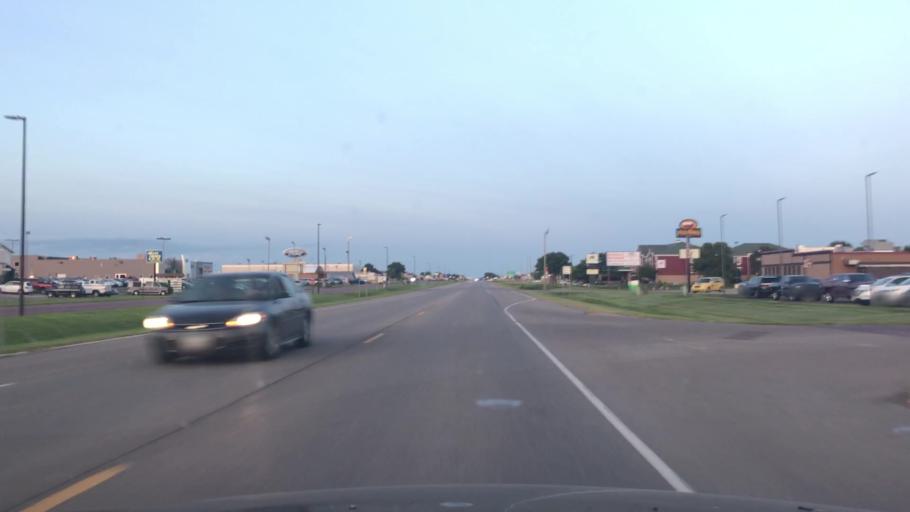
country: US
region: Minnesota
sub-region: Redwood County
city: Redwood Falls
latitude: 44.5414
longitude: -95.0950
